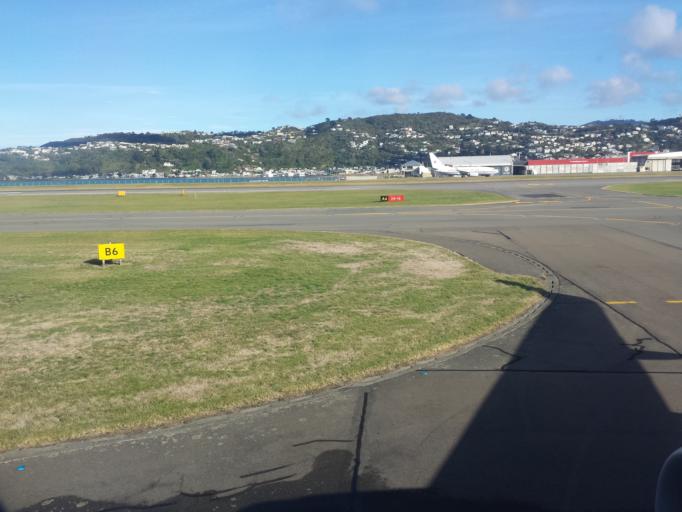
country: NZ
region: Wellington
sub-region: Wellington City
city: Wellington
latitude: -41.3285
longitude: 174.8090
